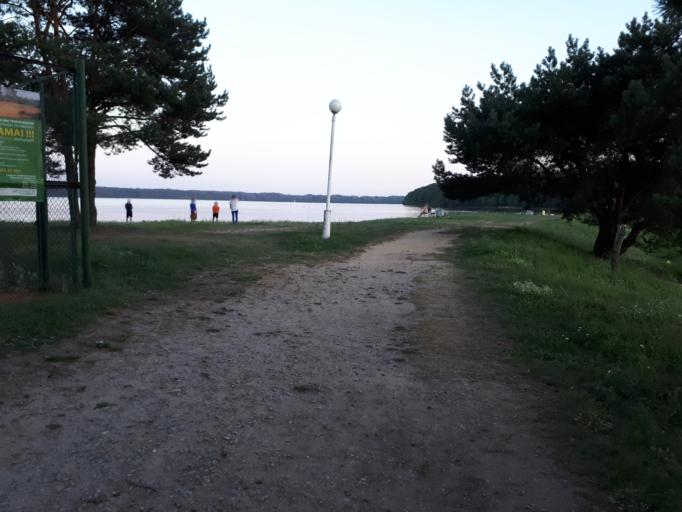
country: LT
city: Ramuciai
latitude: 54.8851
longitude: 24.0265
